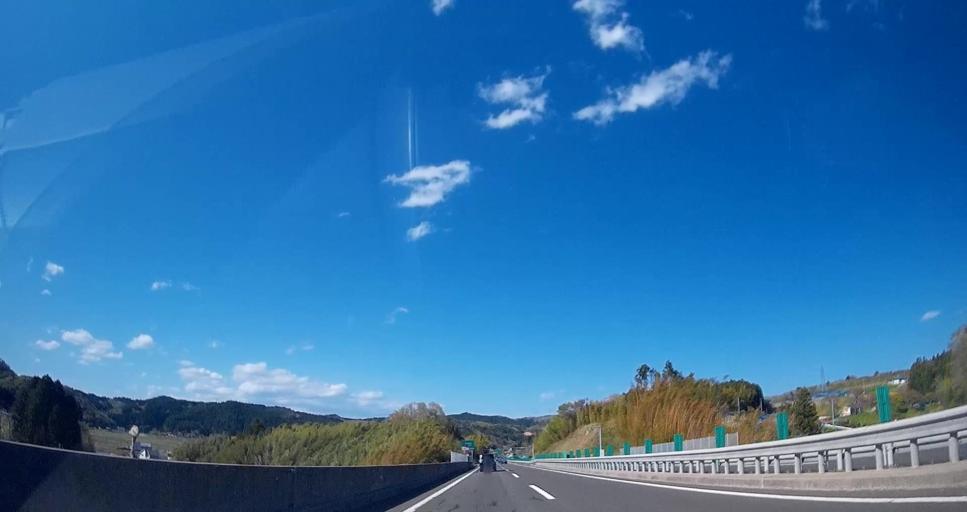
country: JP
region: Miyagi
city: Rifu
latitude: 38.3335
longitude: 140.9970
